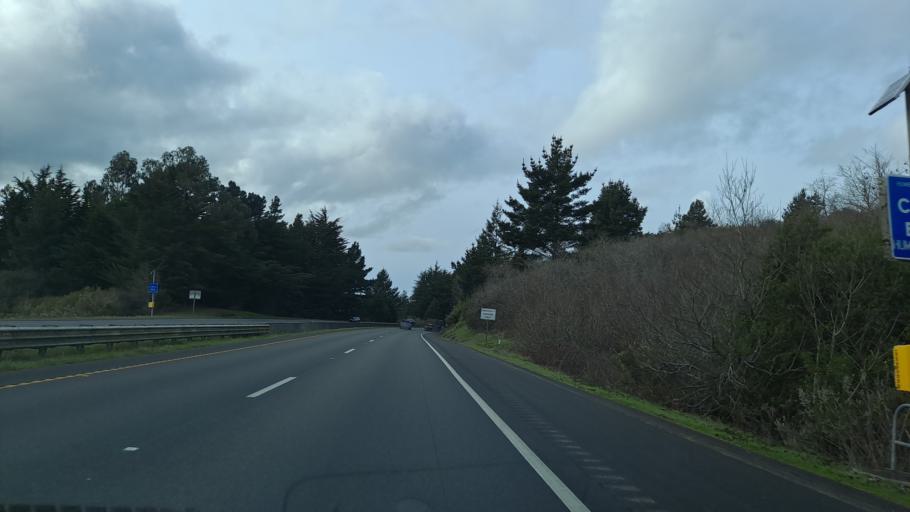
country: US
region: California
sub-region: Humboldt County
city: Fortuna
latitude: 40.6170
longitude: -124.1996
